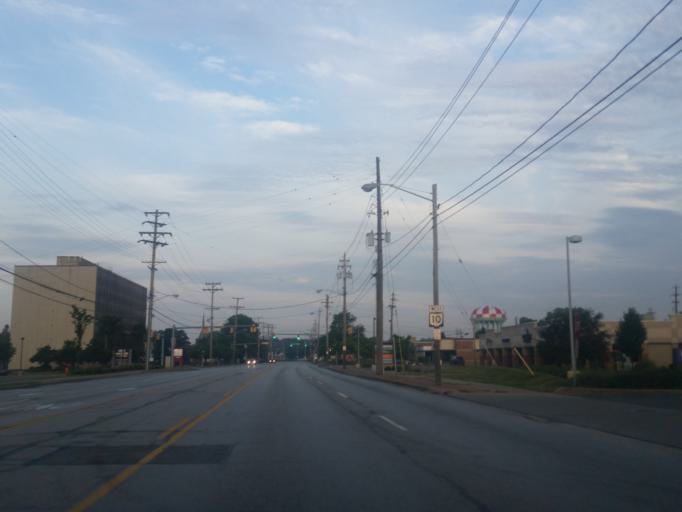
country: US
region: Ohio
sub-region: Cuyahoga County
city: North Olmsted
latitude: 41.4188
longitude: -81.9158
